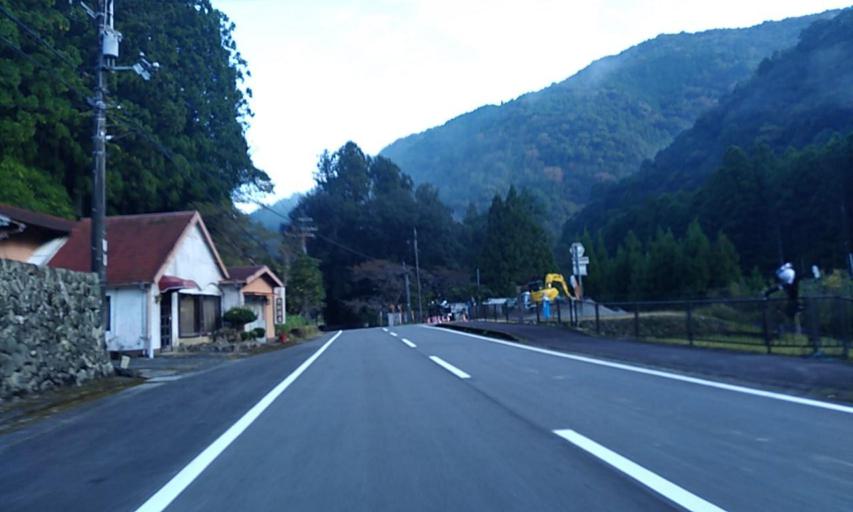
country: JP
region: Wakayama
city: Shingu
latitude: 33.7314
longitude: 135.9106
